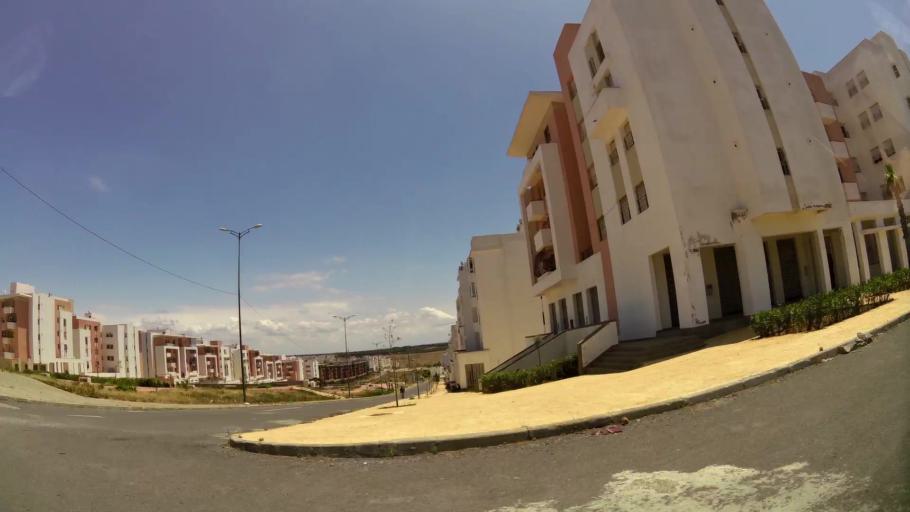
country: MA
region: Gharb-Chrarda-Beni Hssen
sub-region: Kenitra Province
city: Kenitra
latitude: 34.2531
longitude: -6.6582
